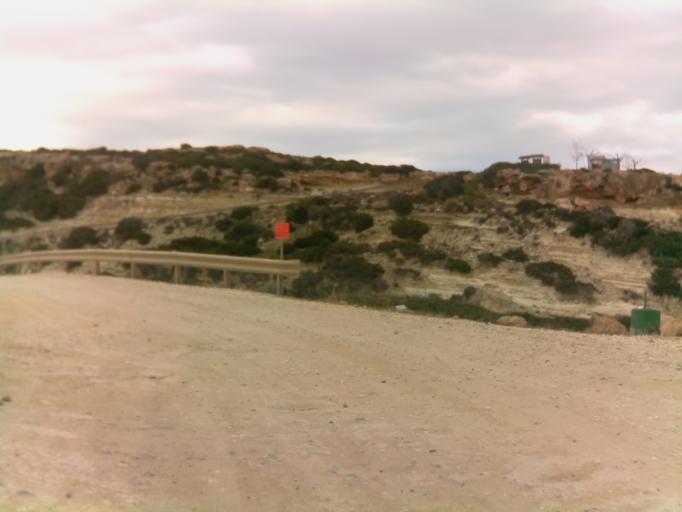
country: CY
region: Pafos
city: Pegeia
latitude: 34.9129
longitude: 32.3271
